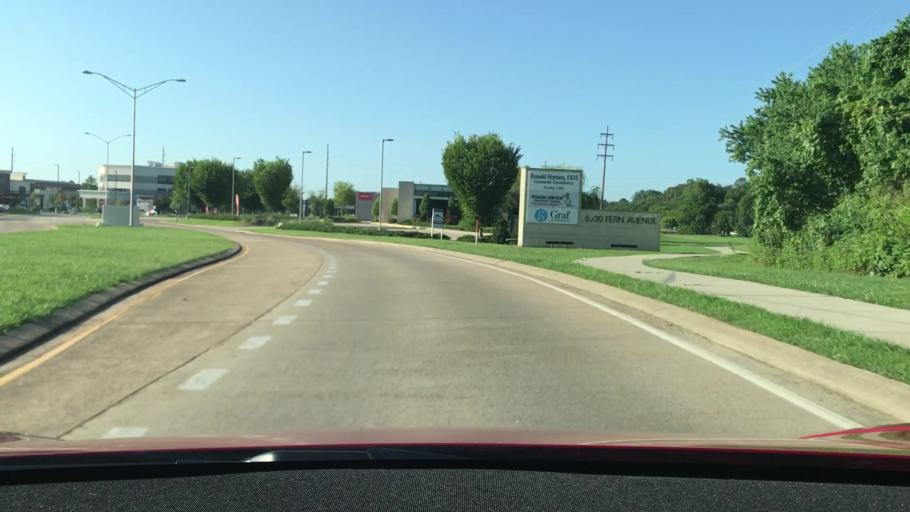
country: US
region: Louisiana
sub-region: Bossier Parish
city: Bossier City
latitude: 32.4466
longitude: -93.7309
